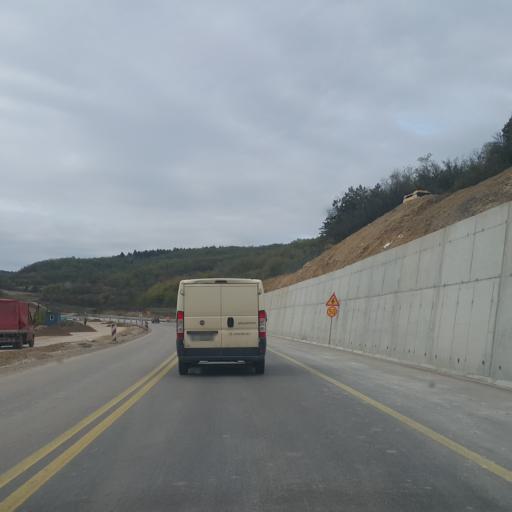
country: RS
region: Central Serbia
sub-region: Pirotski Okrug
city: Bela Palanka
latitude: 43.2325
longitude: 22.4564
